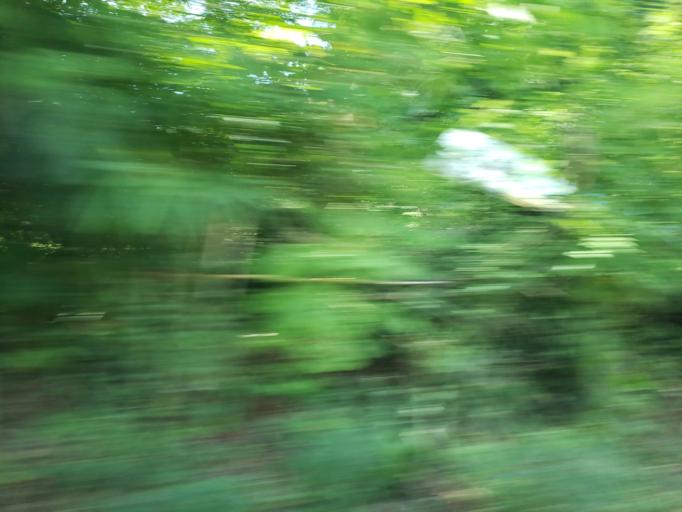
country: ID
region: Bali
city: Kangin
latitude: -8.8208
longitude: 115.1528
